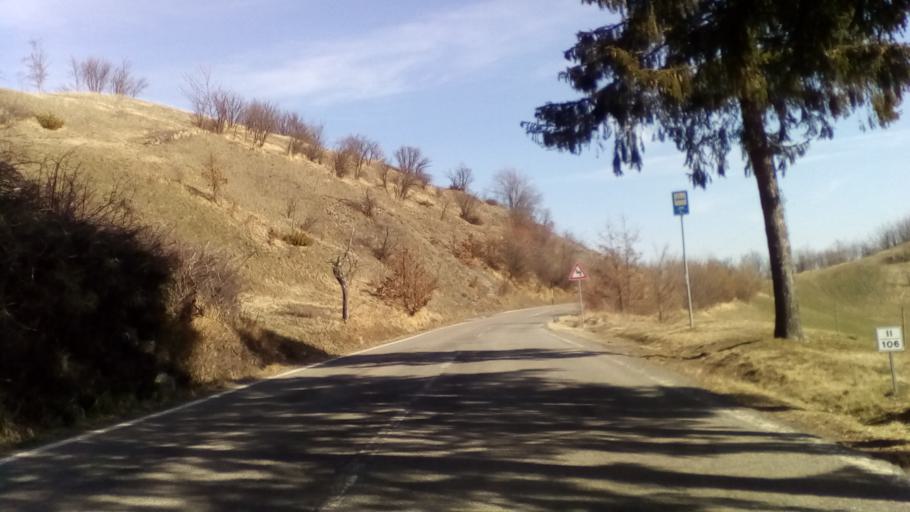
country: IT
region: Emilia-Romagna
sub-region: Provincia di Modena
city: Pievepelago
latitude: 44.2264
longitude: 10.6272
